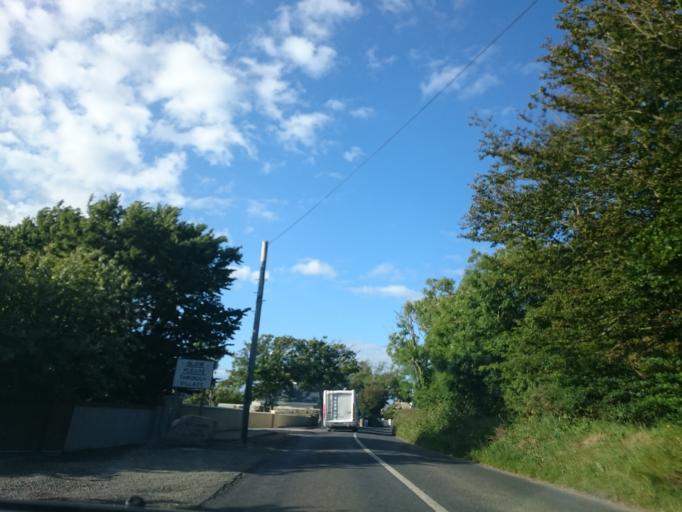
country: IE
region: Leinster
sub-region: Loch Garman
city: Loch Garman
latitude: 52.2013
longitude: -6.5534
